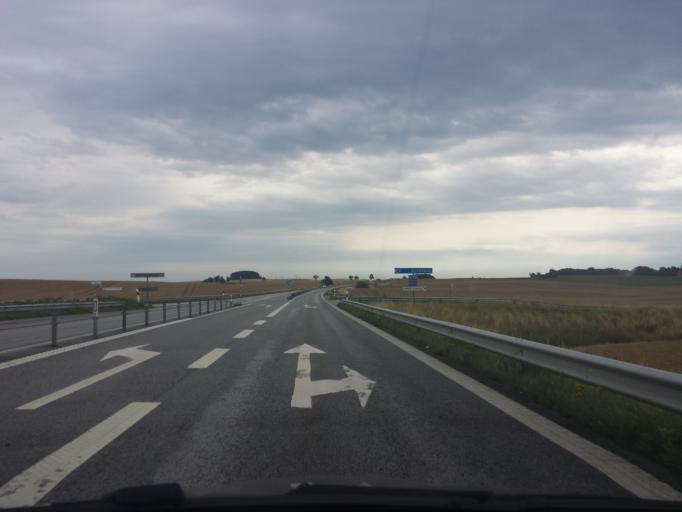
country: SE
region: Skane
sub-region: Skurups Kommun
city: Rydsgard
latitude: 55.4722
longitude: 13.6892
